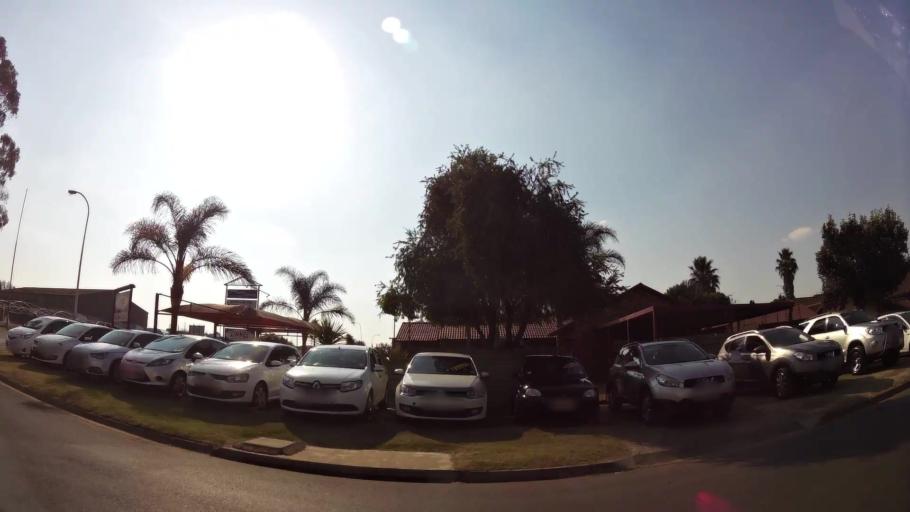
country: ZA
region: Gauteng
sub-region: Ekurhuleni Metropolitan Municipality
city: Boksburg
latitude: -26.1873
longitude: 28.2530
